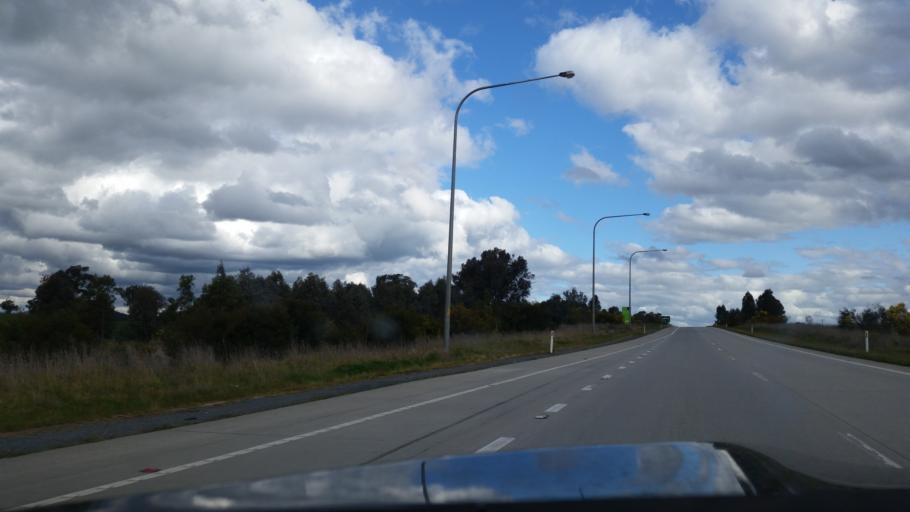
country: AU
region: New South Wales
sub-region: Greater Hume Shire
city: Jindera
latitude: -35.9386
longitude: 147.0033
